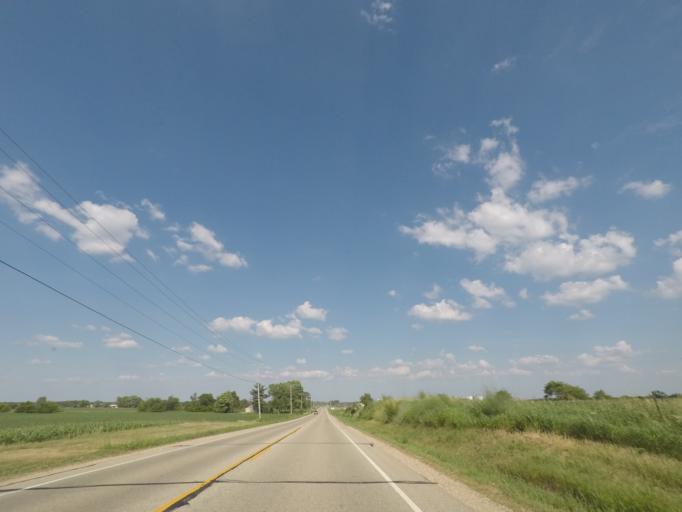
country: US
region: Wisconsin
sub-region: Walworth County
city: East Troy
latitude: 42.7927
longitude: -88.4518
